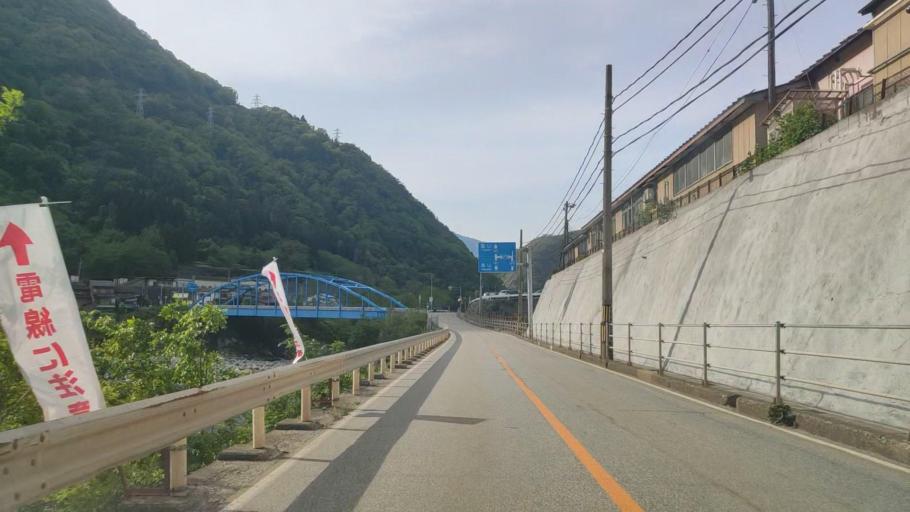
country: JP
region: Gifu
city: Takayama
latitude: 36.3388
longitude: 137.2973
